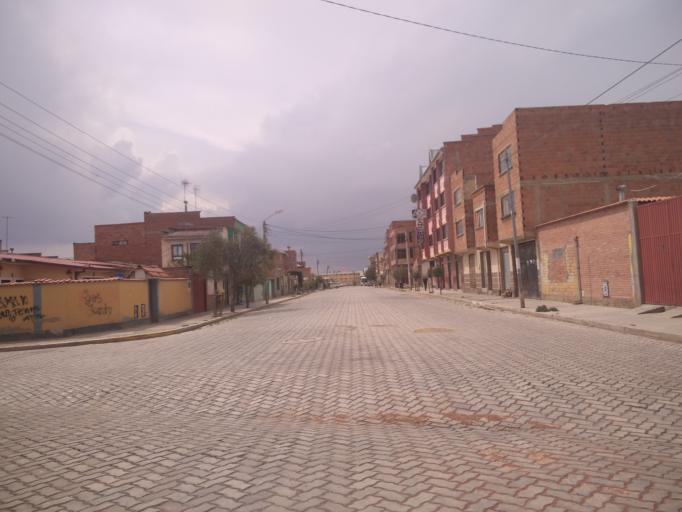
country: BO
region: La Paz
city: La Paz
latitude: -16.5362
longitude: -68.1974
